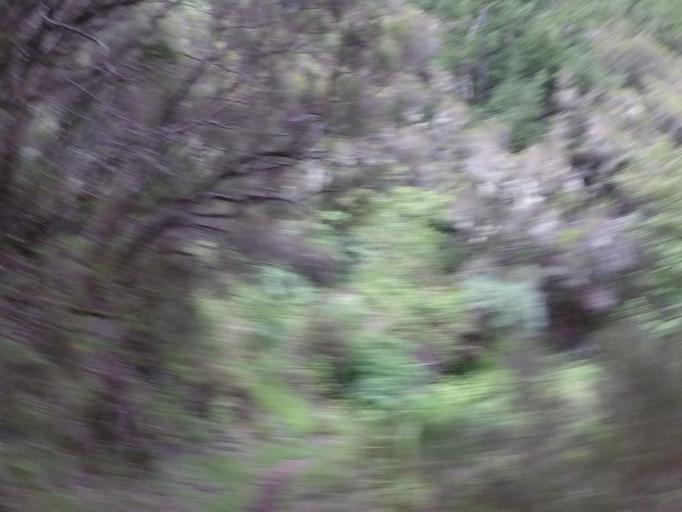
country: PT
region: Madeira
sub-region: Camara de Lobos
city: Curral das Freiras
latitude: 32.7364
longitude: -16.9933
